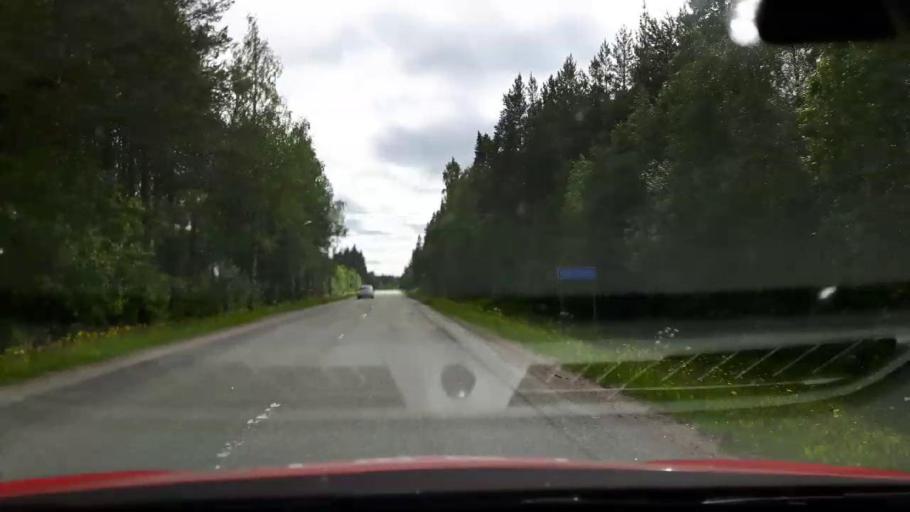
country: SE
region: Jaemtland
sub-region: Ragunda Kommun
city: Hammarstrand
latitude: 62.9892
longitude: 16.0930
